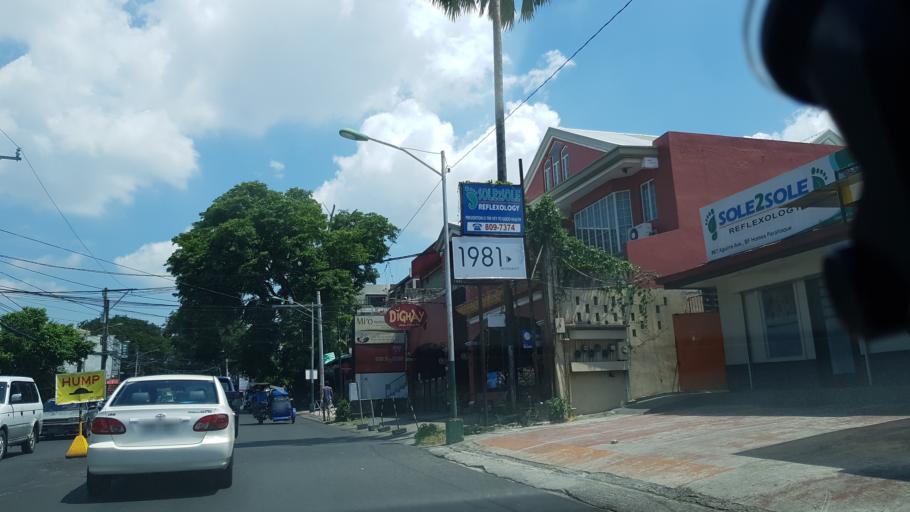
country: PH
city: Sambayanihan People's Village
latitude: 14.4453
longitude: 121.0231
